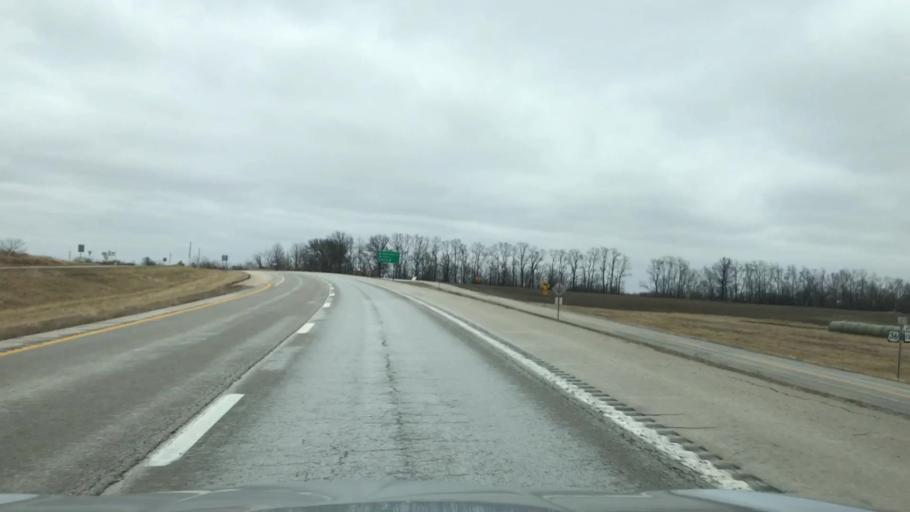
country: US
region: Missouri
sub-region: Livingston County
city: Chillicothe
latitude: 39.7366
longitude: -93.6316
